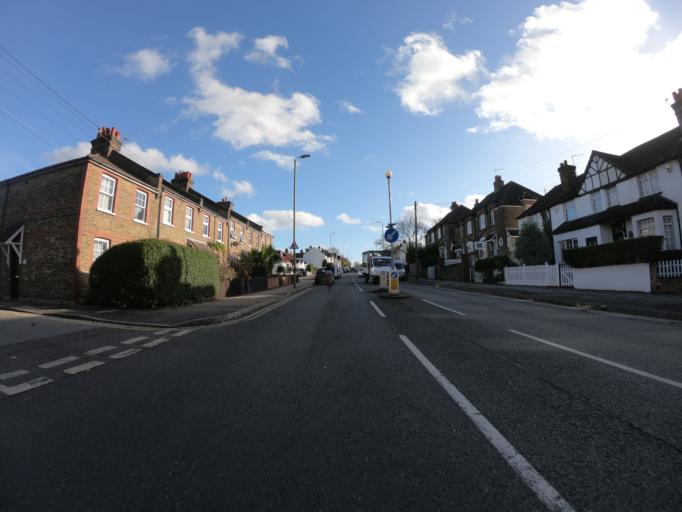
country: GB
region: England
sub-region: Greater London
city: Chislehurst
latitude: 51.4242
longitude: 0.0592
